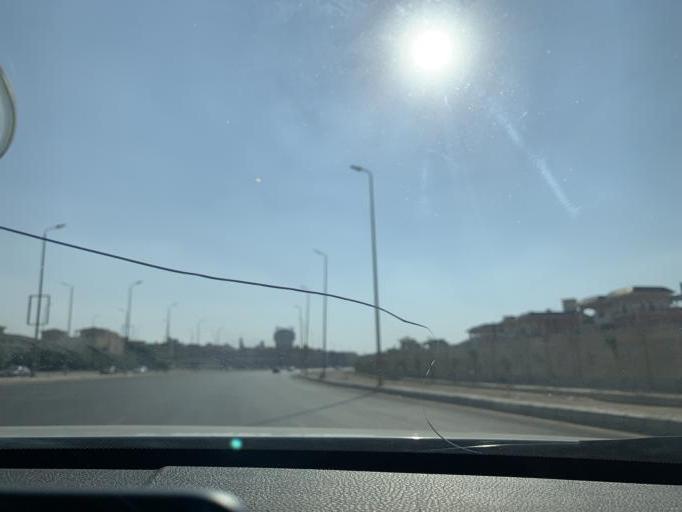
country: EG
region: Muhafazat al Qalyubiyah
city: Al Khankah
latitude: 30.0123
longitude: 31.4744
